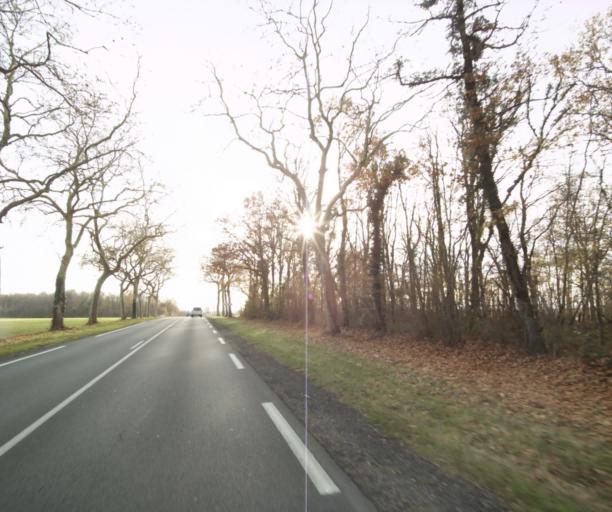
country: FR
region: Poitou-Charentes
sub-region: Departement de la Charente-Maritime
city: Saint-Hilaire-de-Villefranche
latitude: 45.8187
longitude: -0.5456
